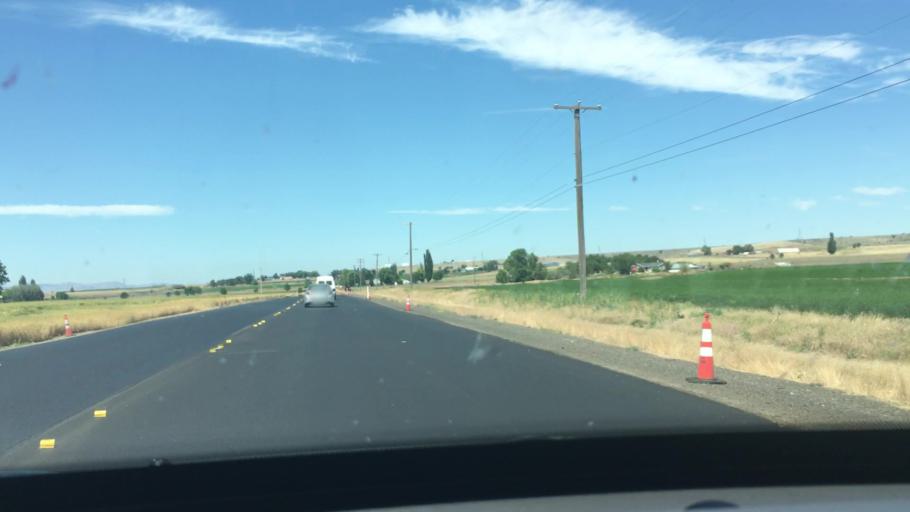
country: US
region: Oregon
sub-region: Jefferson County
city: Culver
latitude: 44.5493
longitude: -121.1692
